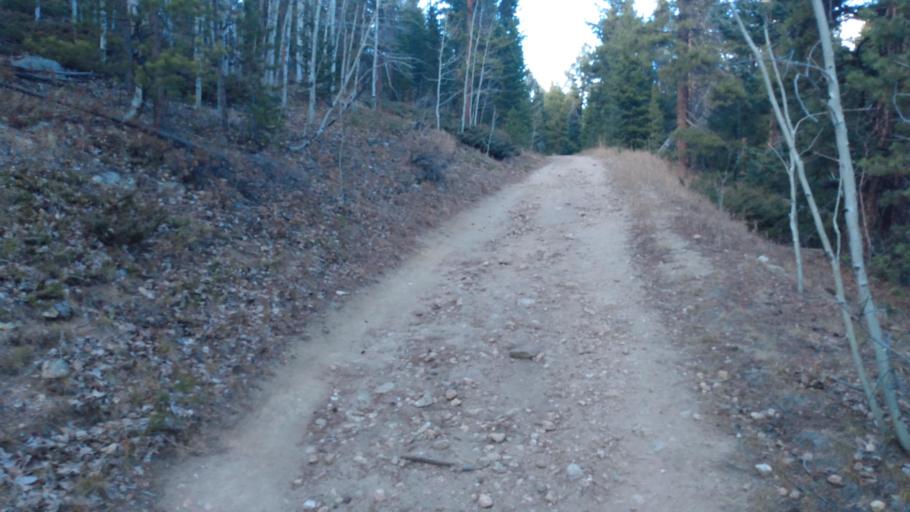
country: US
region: Colorado
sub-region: Boulder County
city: Nederland
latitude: 39.9602
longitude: -105.4483
